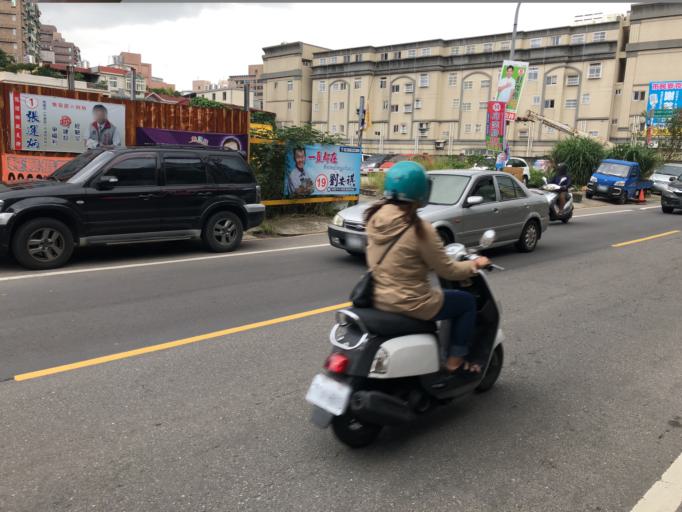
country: TW
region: Taiwan
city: Taoyuan City
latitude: 24.9649
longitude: 121.2523
